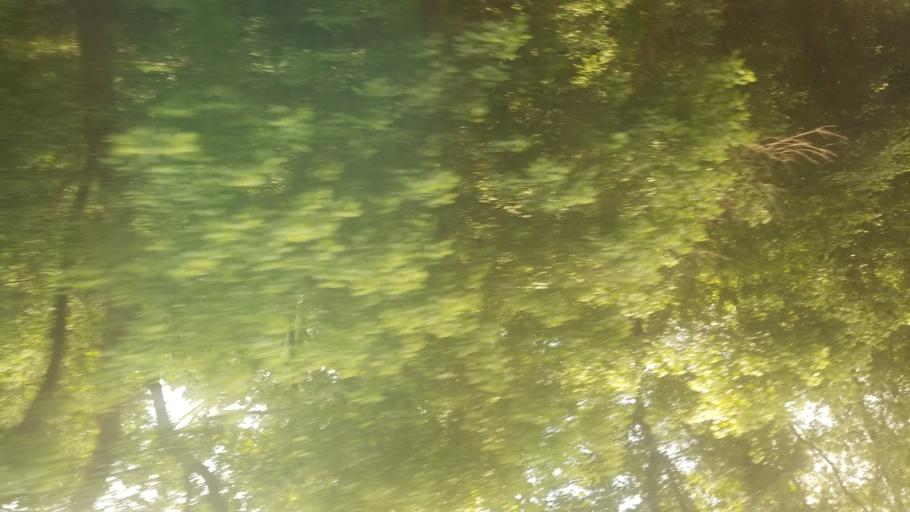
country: US
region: Maryland
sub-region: Frederick County
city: Point of Rocks
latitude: 39.3106
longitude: -77.5648
